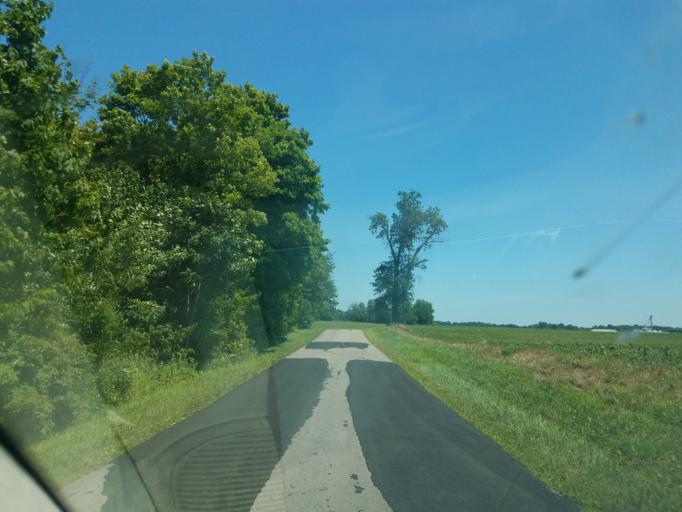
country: US
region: Ohio
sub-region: Hardin County
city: Forest
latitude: 40.8002
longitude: -83.5305
